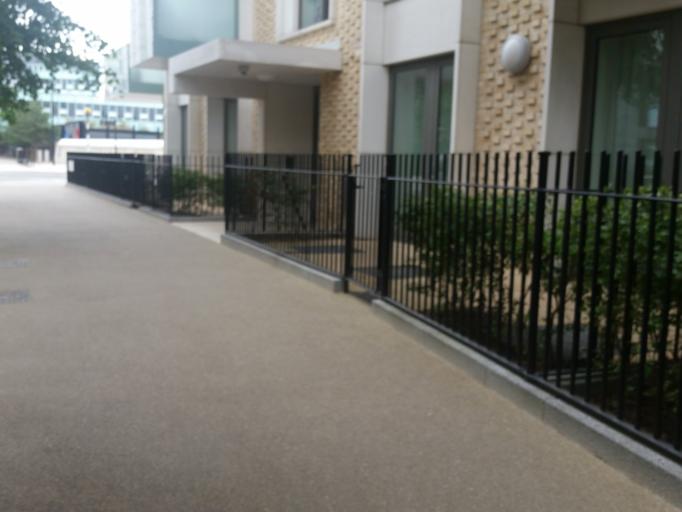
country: GB
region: England
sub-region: Greater London
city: Poplar
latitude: 51.5479
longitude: -0.0055
